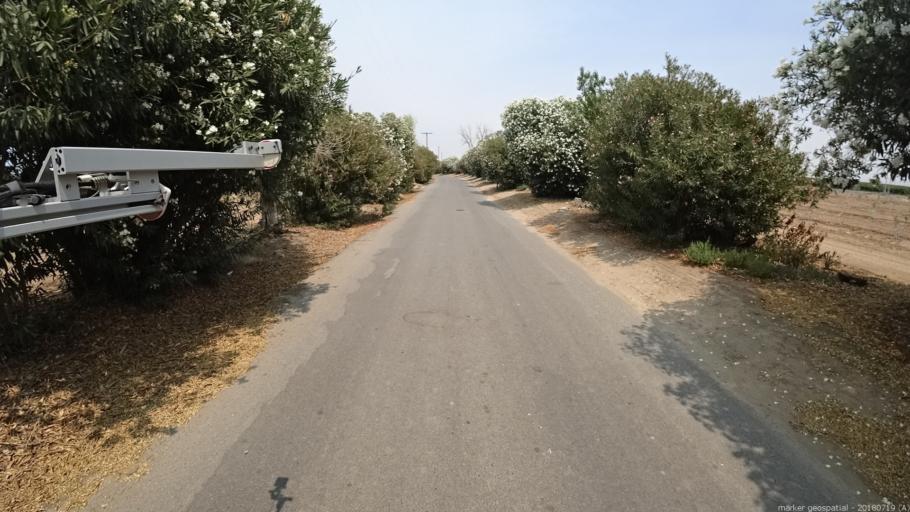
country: US
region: California
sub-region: Madera County
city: Fairmead
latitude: 37.0943
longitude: -120.1291
